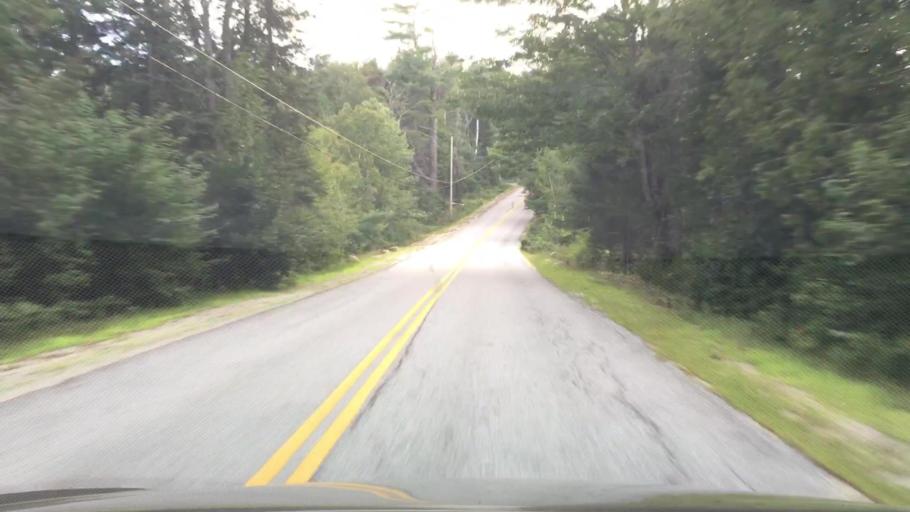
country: US
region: Maine
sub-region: Hancock County
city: Penobscot
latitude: 44.4457
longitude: -68.6241
